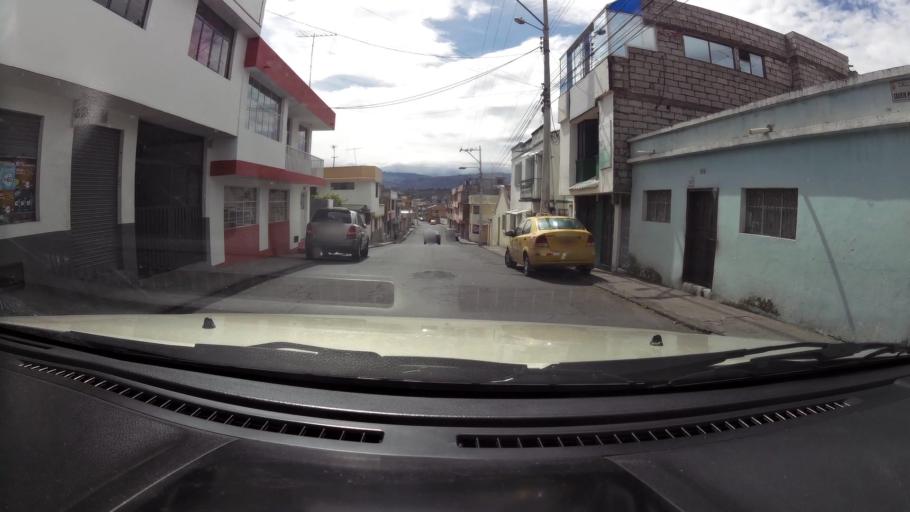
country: EC
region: Cotopaxi
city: Latacunga
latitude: -0.9226
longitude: -78.6212
